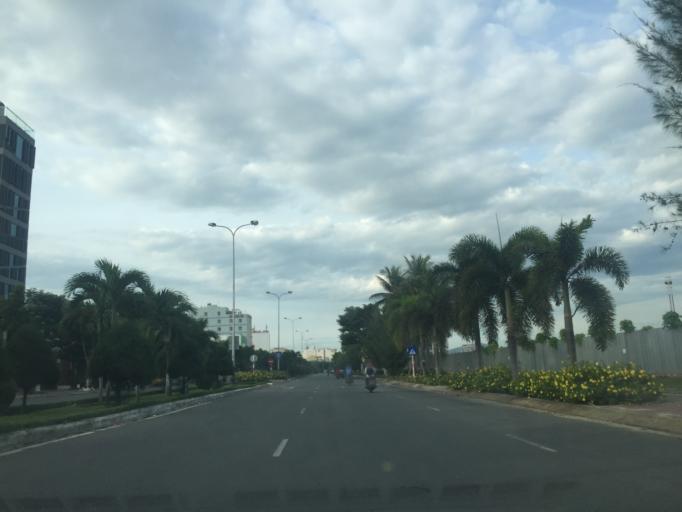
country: VN
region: Da Nang
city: Da Nang
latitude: 16.0866
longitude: 108.2147
